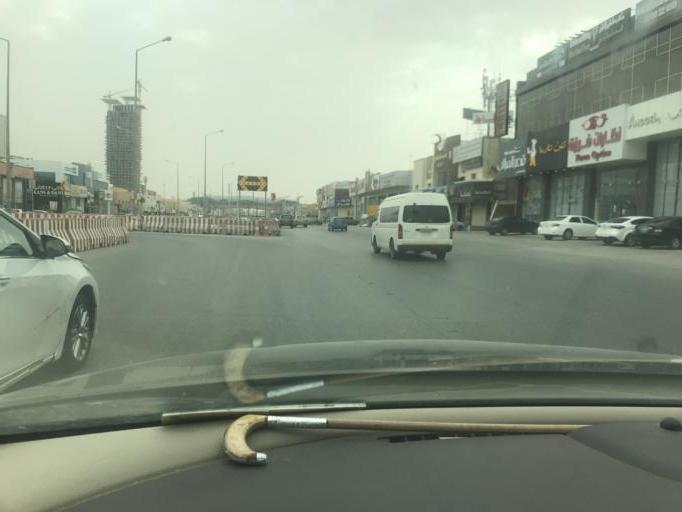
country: SA
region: Ar Riyad
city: Riyadh
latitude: 24.8140
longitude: 46.6311
